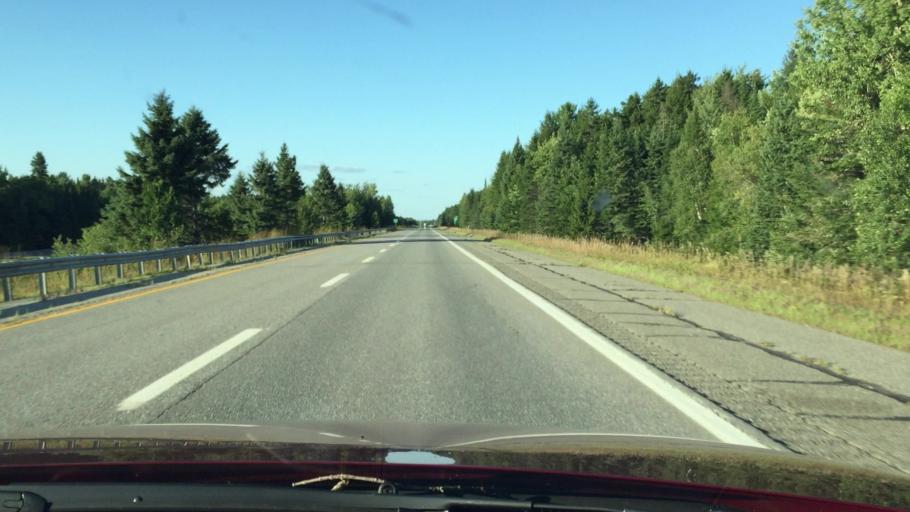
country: US
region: Maine
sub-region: Penobscot County
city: Patten
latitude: 45.8506
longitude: -68.4271
